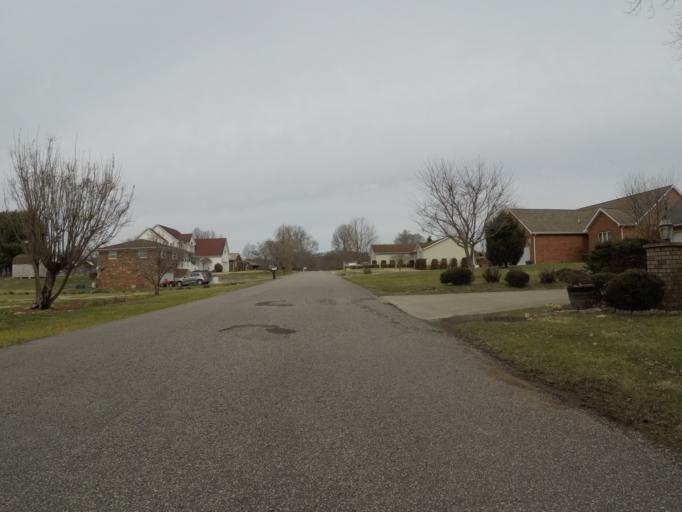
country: US
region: West Virginia
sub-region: Cabell County
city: Pea Ridge
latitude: 38.4443
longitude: -82.3427
